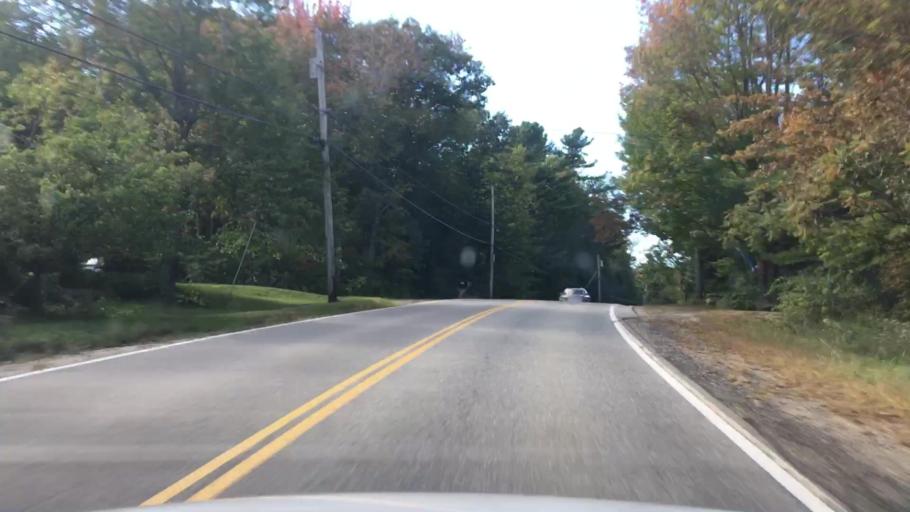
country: US
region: Maine
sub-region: Sagadahoc County
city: Topsham
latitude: 43.9354
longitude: -70.0177
